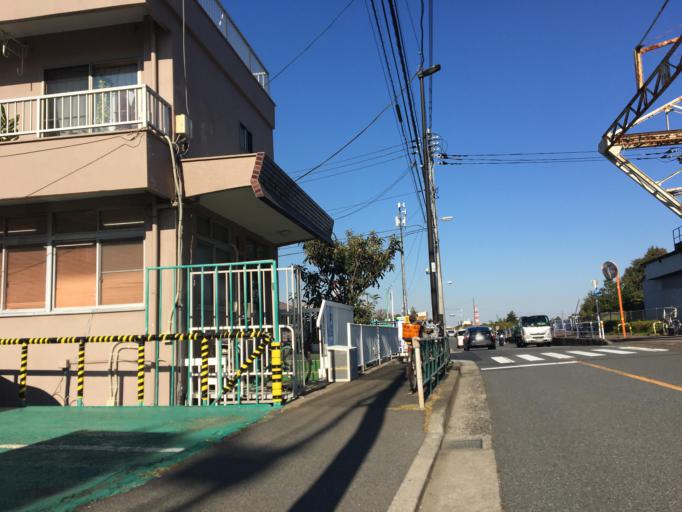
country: JP
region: Tokyo
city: Urayasu
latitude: 35.6962
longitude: 139.9165
